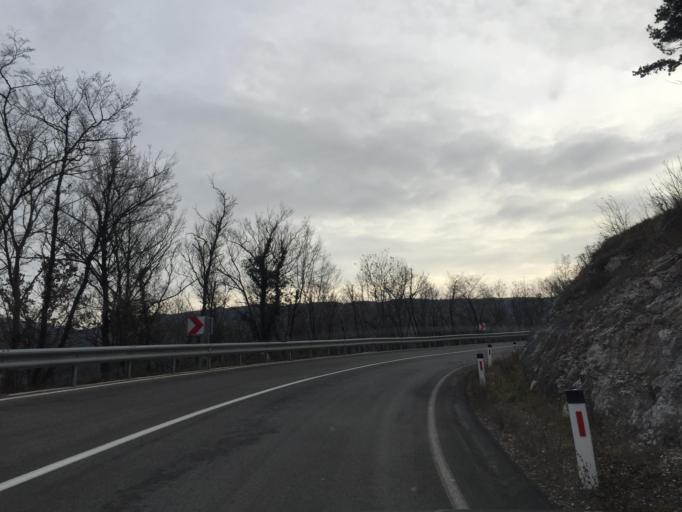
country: SI
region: Nova Gorica
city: Solkan
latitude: 45.9899
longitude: 13.6718
